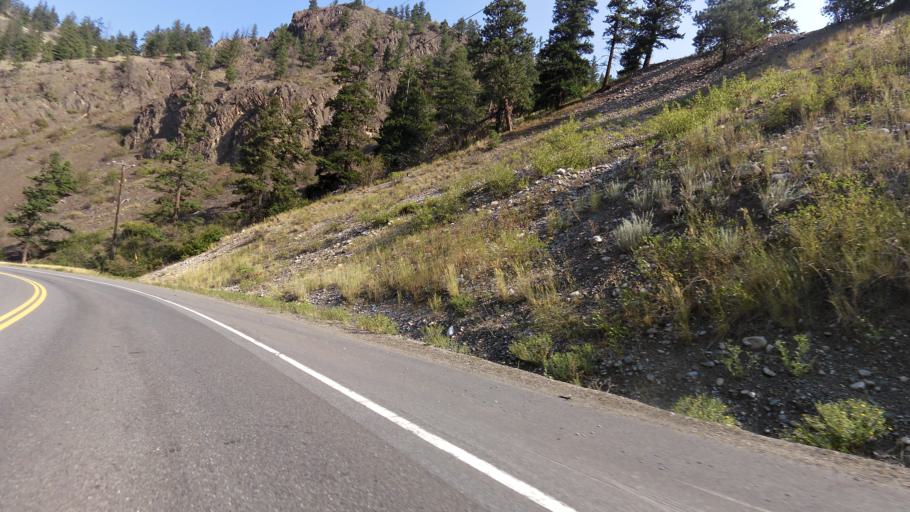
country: CA
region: British Columbia
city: Princeton
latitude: 49.3603
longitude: -120.1003
